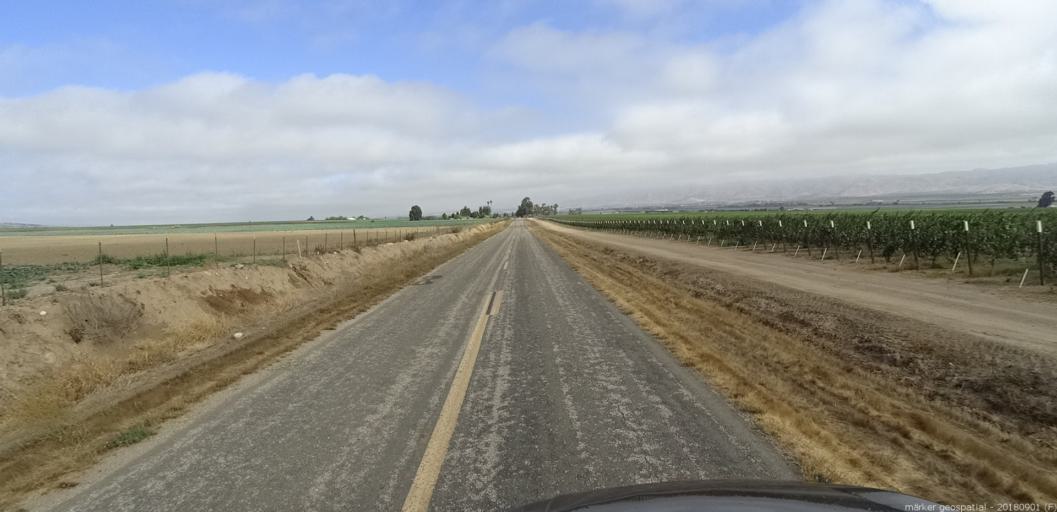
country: US
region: California
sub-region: Monterey County
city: Soledad
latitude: 36.3659
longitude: -121.3359
